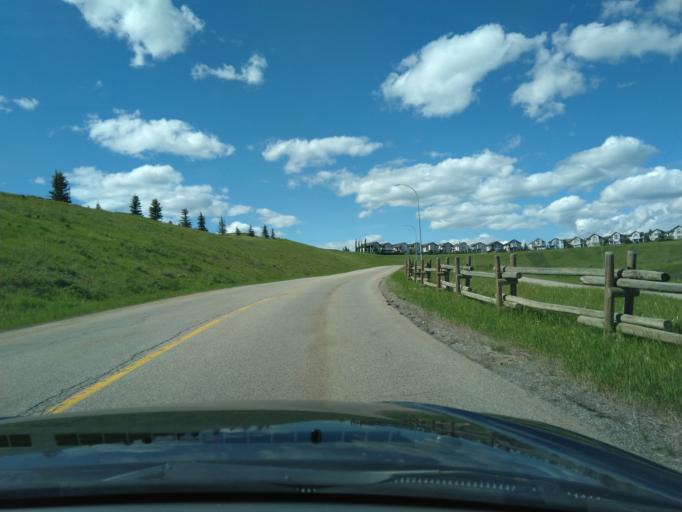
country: CA
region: Alberta
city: Cochrane
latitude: 51.1918
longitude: -114.4267
